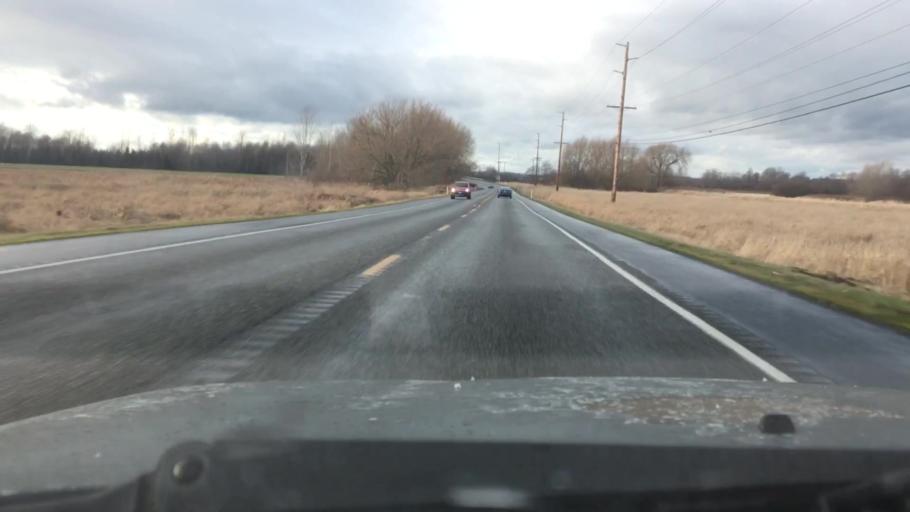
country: US
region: Washington
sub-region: Whatcom County
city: Marietta
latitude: 48.8180
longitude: -122.5720
